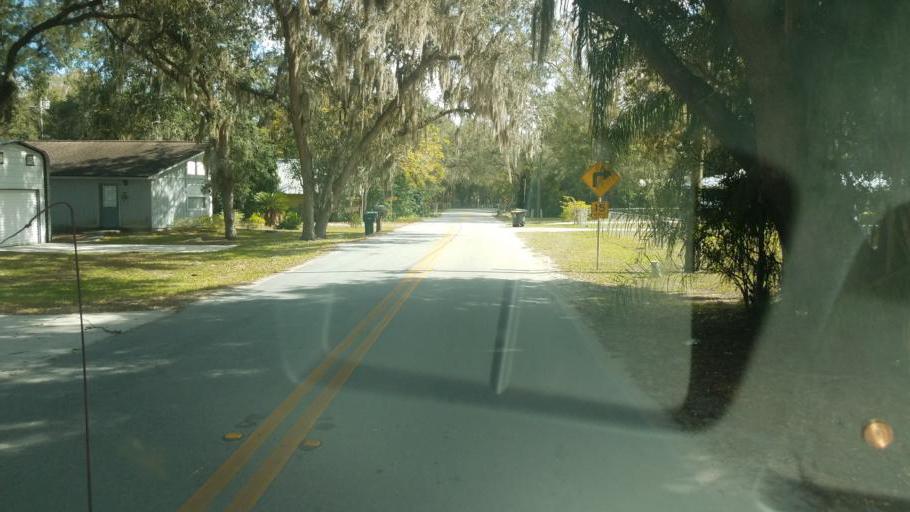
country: US
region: Florida
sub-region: Osceola County
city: Poinciana
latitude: 27.9767
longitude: -81.3757
